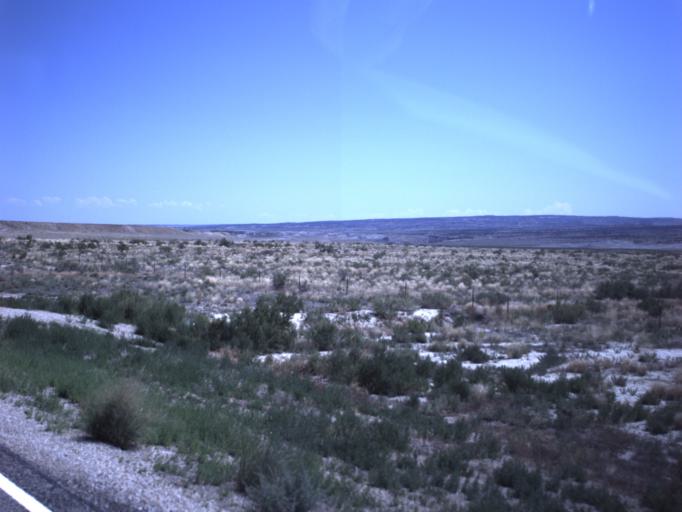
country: US
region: Utah
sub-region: Emery County
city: Ferron
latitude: 38.8450
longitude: -111.3119
